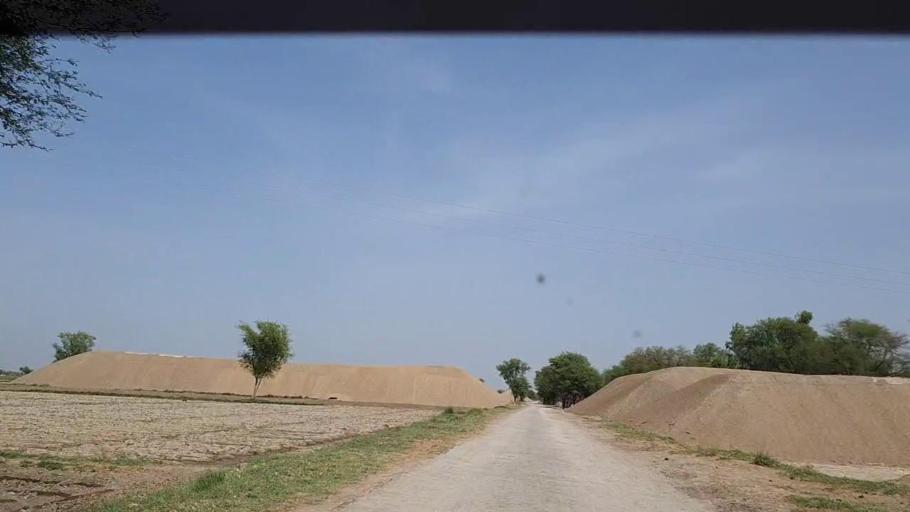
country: PK
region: Sindh
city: Phulji
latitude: 26.9575
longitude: 67.7054
